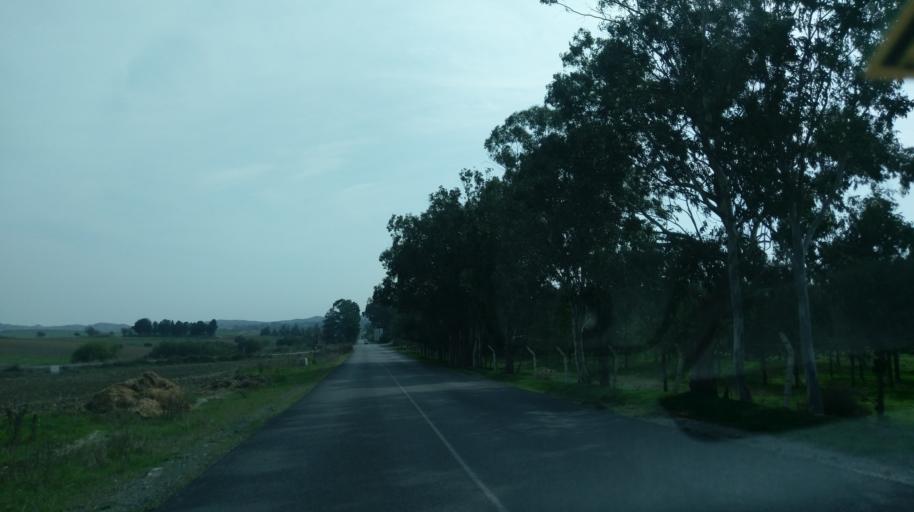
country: CY
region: Keryneia
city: Lapithos
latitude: 35.2793
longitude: 33.1050
